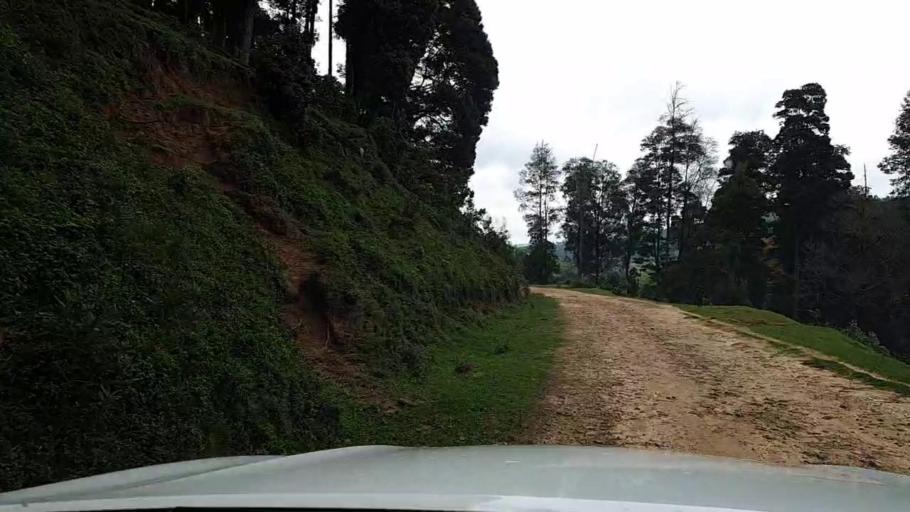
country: RW
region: Western Province
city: Kibuye
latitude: -2.2906
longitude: 29.3689
